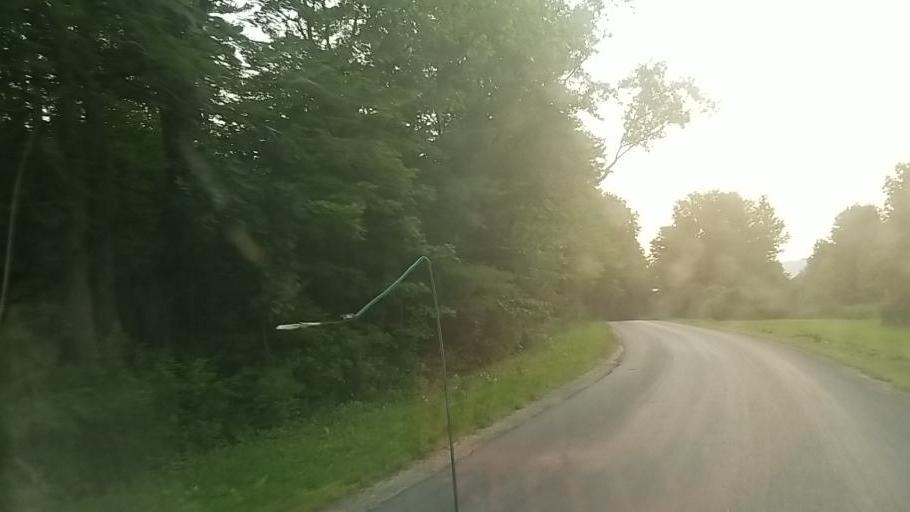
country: US
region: New York
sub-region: Montgomery County
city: Fonda
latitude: 42.9166
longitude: -74.4044
